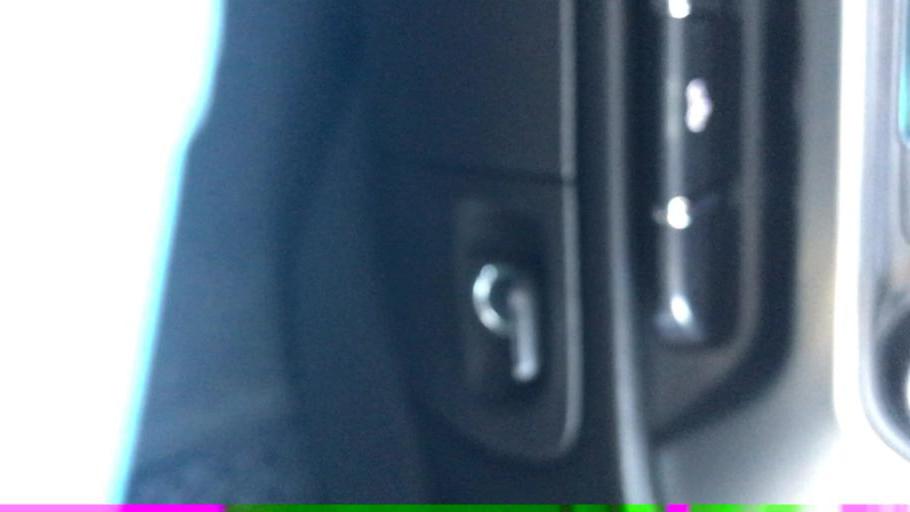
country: US
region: Texas
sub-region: Denton County
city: Double Oak
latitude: 33.0466
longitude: -97.1098
